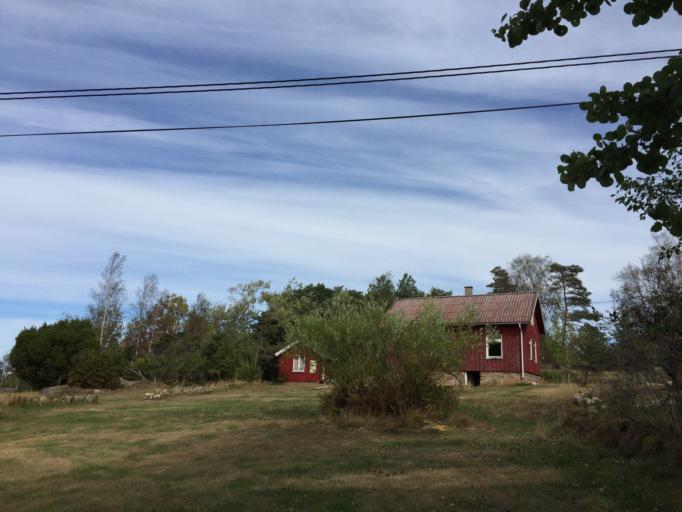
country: NO
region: Ostfold
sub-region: Fredrikstad
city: Fredrikstad
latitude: 59.0994
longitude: 10.9272
